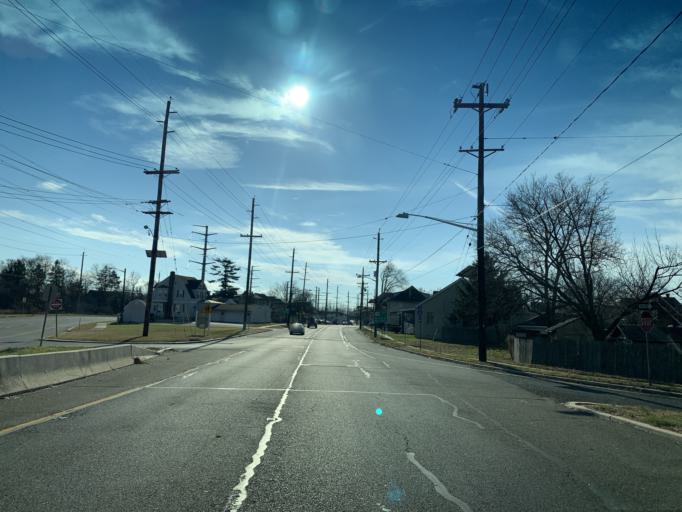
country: US
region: New Jersey
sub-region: Camden County
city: Brooklawn
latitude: 39.8740
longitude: -75.1270
